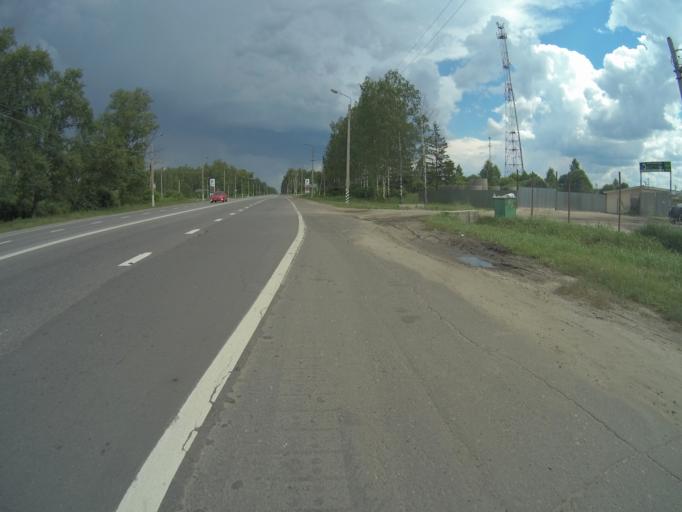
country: RU
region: Vladimir
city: Orgtrud
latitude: 56.2077
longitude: 40.6788
